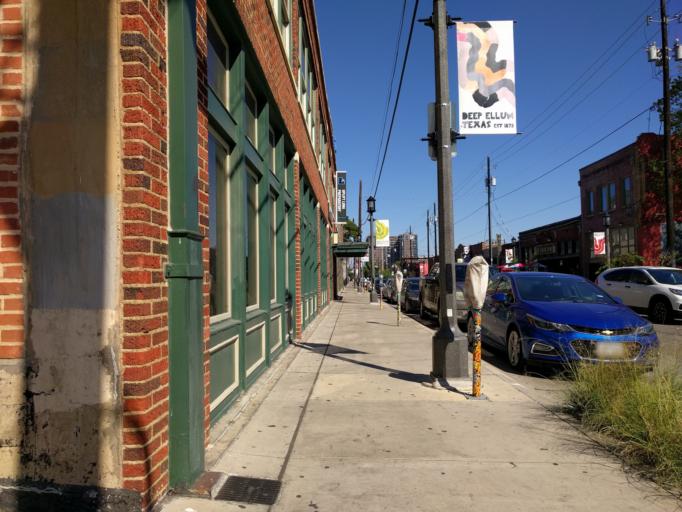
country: US
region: Texas
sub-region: Dallas County
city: Dallas
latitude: 32.7843
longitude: -96.7856
